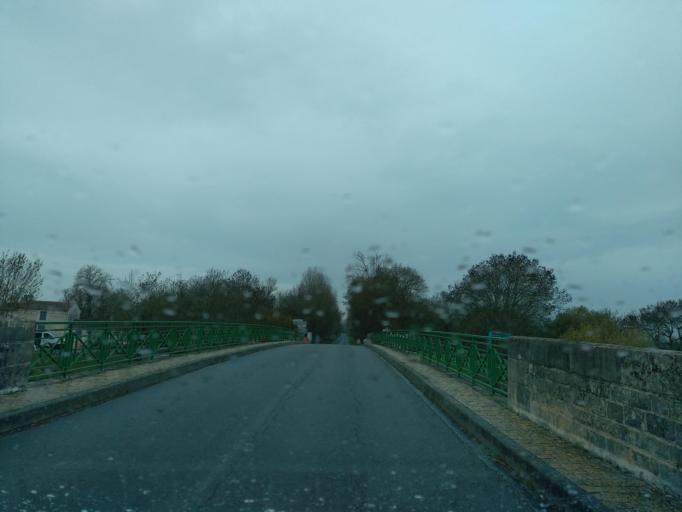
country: FR
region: Pays de la Loire
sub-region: Departement de la Vendee
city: Maillezais
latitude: 46.3212
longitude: -0.7874
